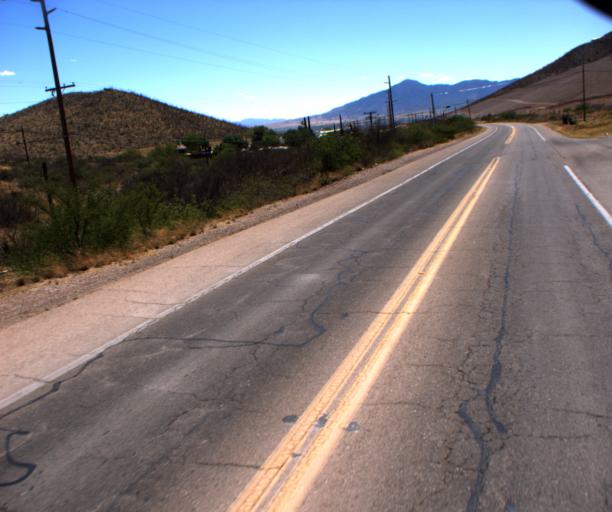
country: US
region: Arizona
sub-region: Cochise County
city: Bisbee
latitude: 31.4170
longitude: -109.8978
